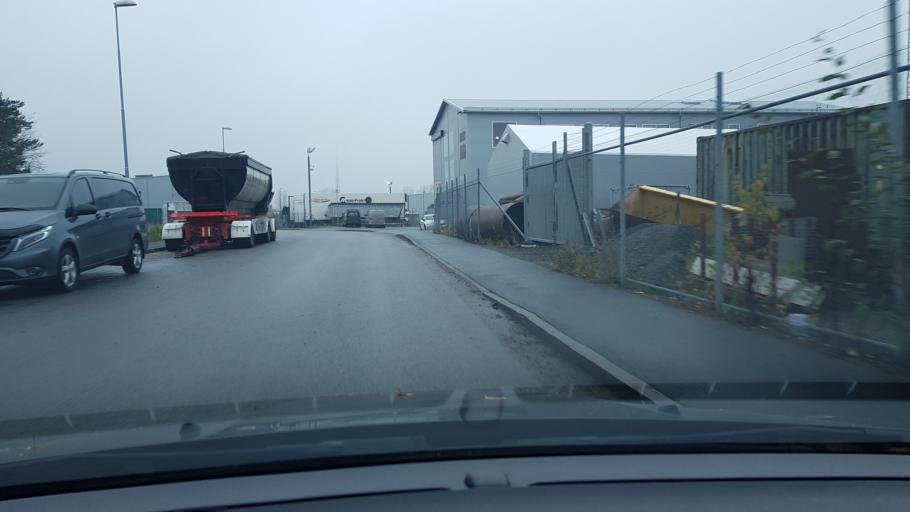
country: SE
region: Uppsala
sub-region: Uppsala Kommun
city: Saevja
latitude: 59.8433
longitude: 17.7264
